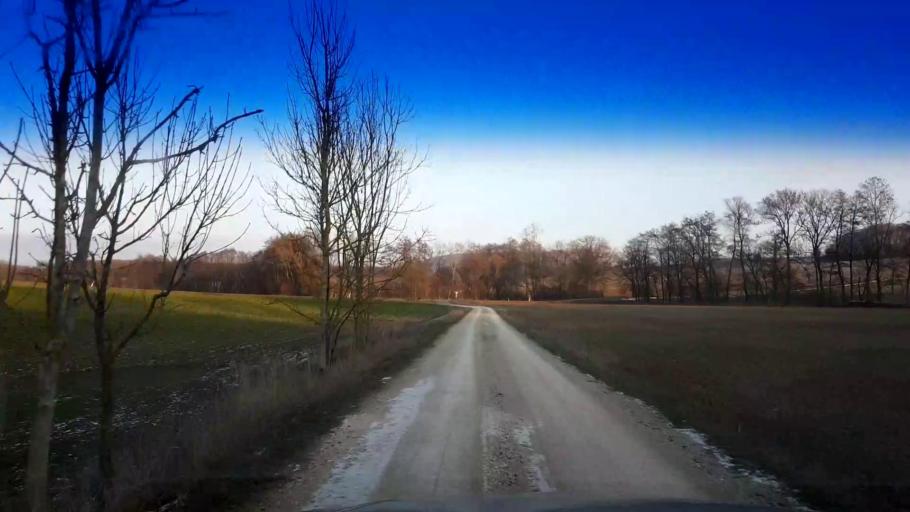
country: DE
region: Bavaria
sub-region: Upper Franconia
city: Schesslitz
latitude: 49.9876
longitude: 11.0086
